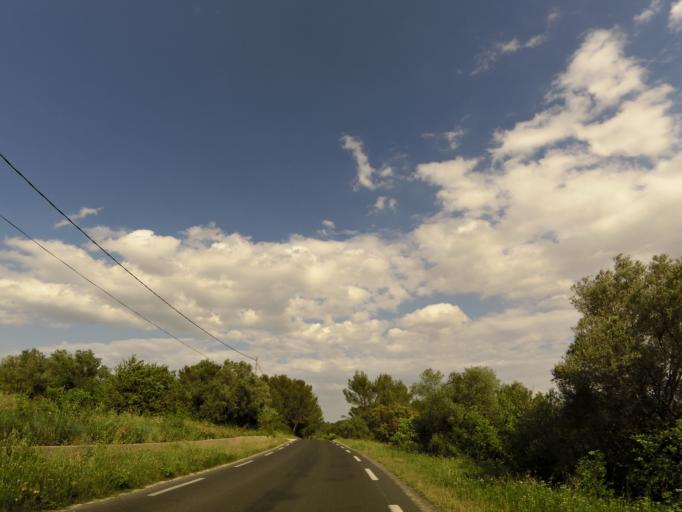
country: FR
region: Languedoc-Roussillon
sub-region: Departement du Gard
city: Aubais
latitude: 43.7488
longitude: 4.1338
